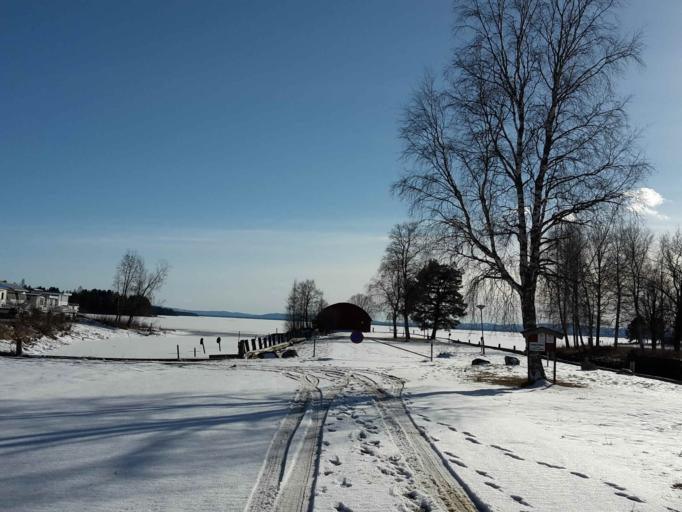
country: SE
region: Dalarna
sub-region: Orsa Kommun
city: Orsa
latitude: 61.1177
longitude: 14.6074
